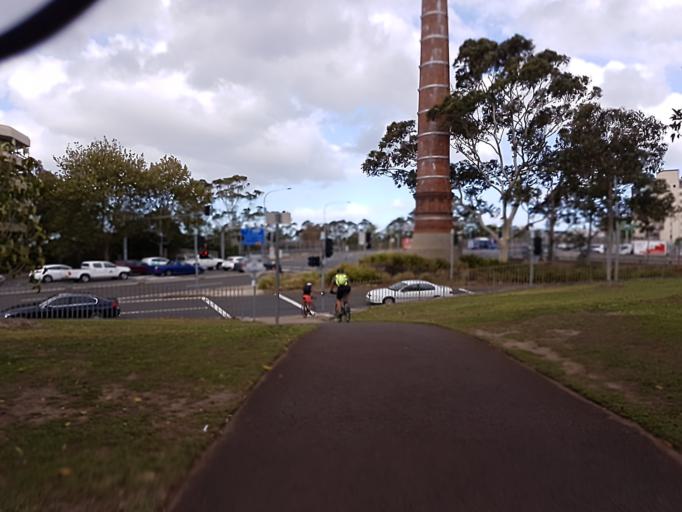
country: AU
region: New South Wales
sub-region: North Sydney
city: Cammeray
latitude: -33.8299
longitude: 151.2125
